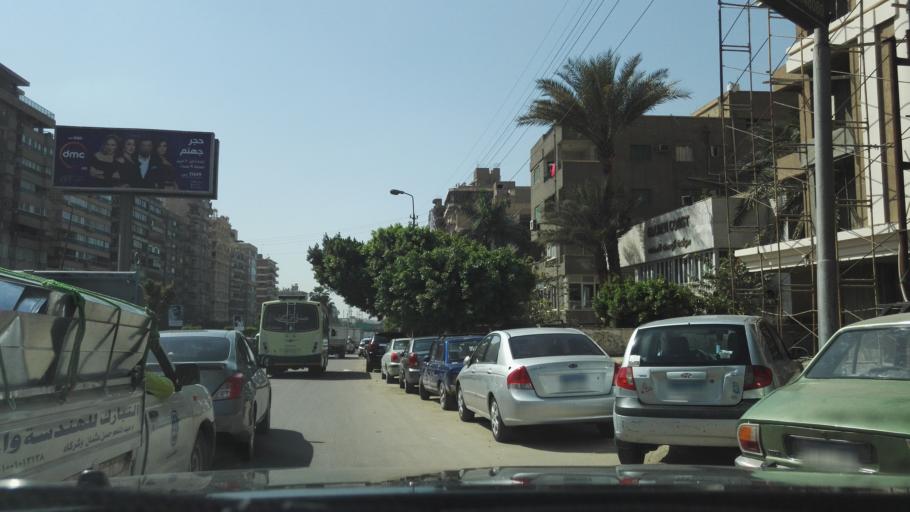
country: EG
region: Muhafazat al Qahirah
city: Cairo
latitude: 30.0820
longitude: 31.3446
